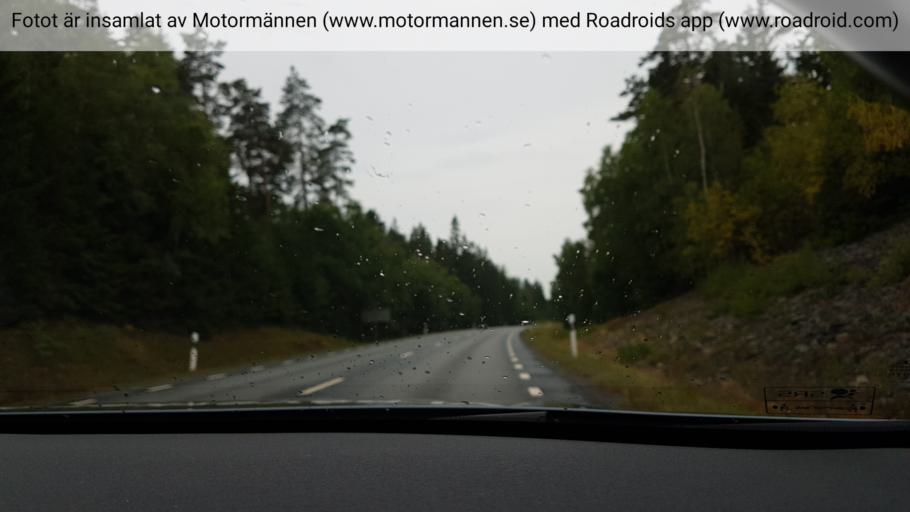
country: SE
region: Joenkoeping
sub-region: Varnamo Kommun
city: Varnamo
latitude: 57.2005
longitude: 14.0912
